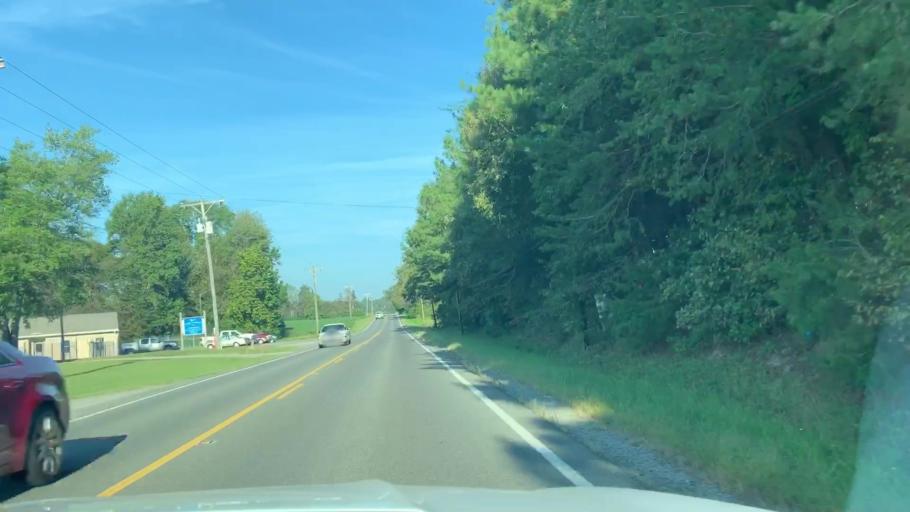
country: US
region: Virginia
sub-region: Lancaster County
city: Lancaster
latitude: 37.7652
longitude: -76.4273
